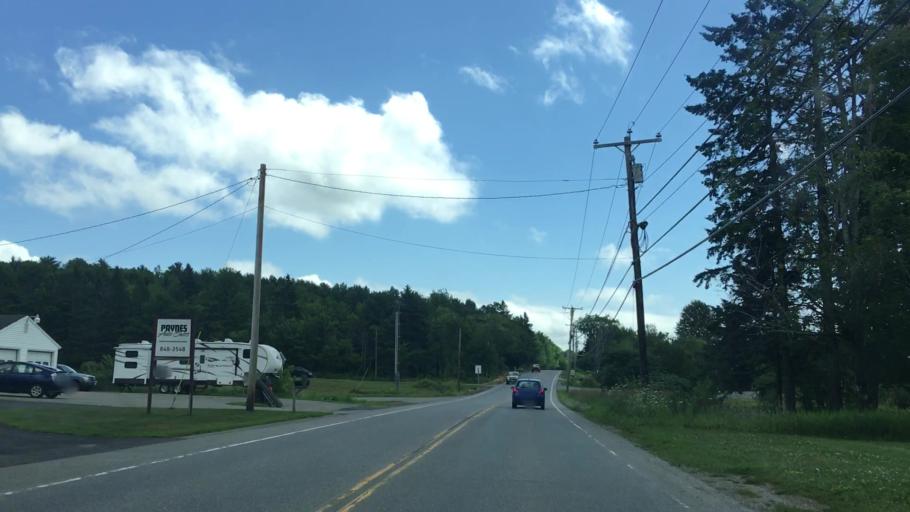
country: US
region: Maine
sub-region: Penobscot County
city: Hermon
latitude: 44.8049
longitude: -68.9003
